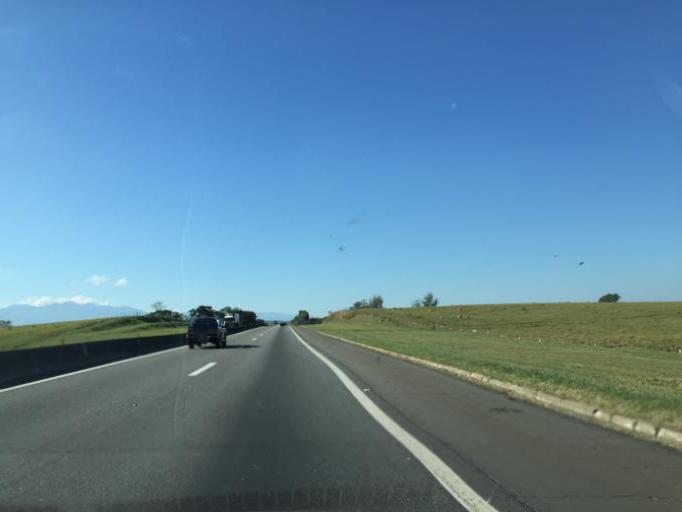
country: BR
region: Sao Paulo
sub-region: Lorena
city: Lorena
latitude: -22.7016
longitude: -45.0360
